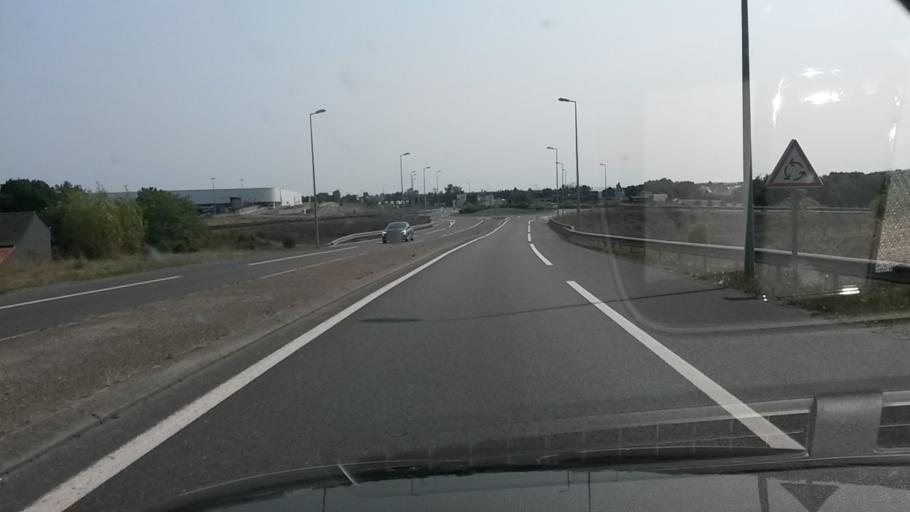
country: FR
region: Pays de la Loire
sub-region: Departement de la Loire-Atlantique
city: Saint-Gereon
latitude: 47.3930
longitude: -1.1890
